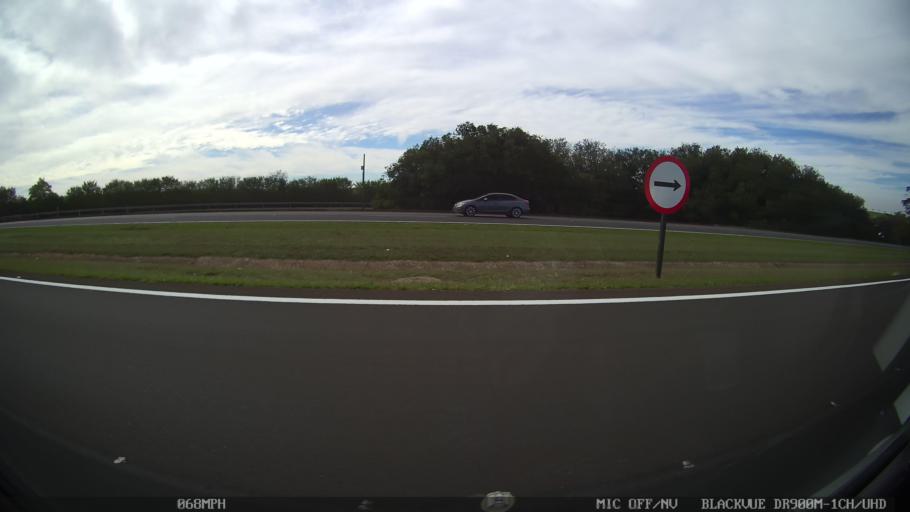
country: BR
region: Sao Paulo
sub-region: Taquaritinga
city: Taquaritinga
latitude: -21.4746
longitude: -48.6003
